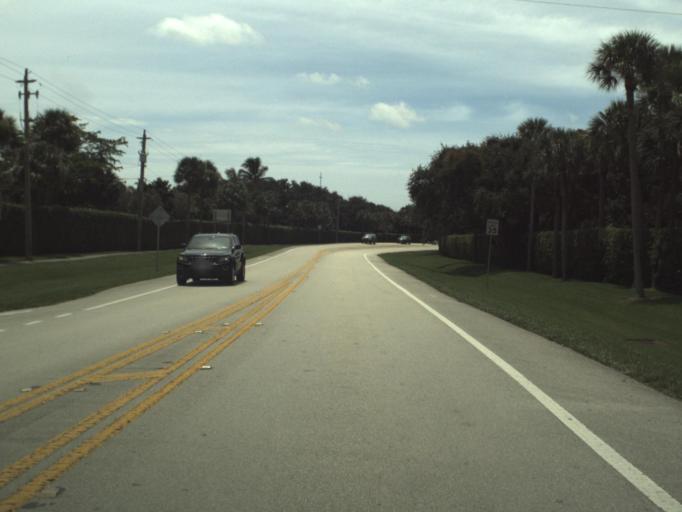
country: US
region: Florida
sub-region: Palm Beach County
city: North Palm Beach
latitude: 26.8388
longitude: -80.0498
